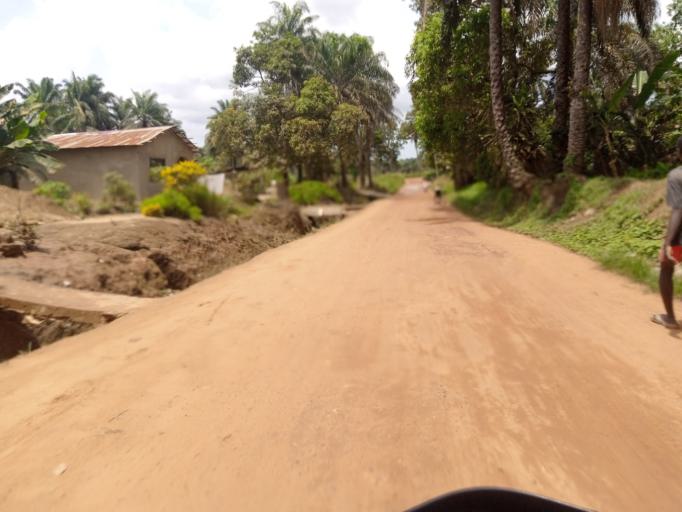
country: SL
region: Western Area
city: Waterloo
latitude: 8.3338
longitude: -13.0046
